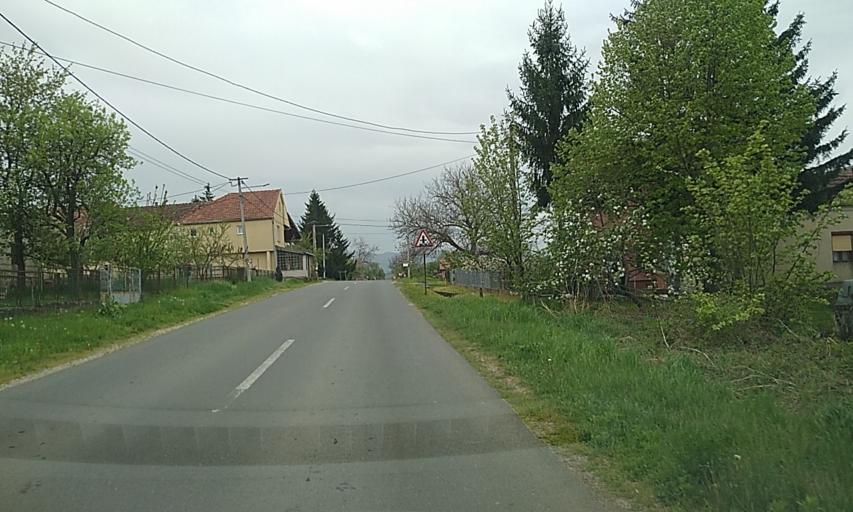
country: RS
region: Central Serbia
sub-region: Nisavski Okrug
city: Razanj
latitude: 43.5745
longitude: 21.5029
